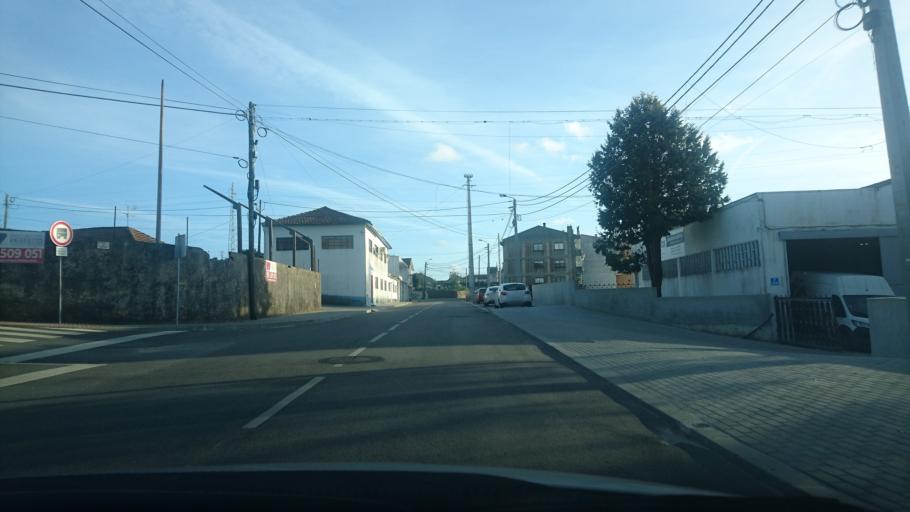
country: PT
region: Aveiro
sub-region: Santa Maria da Feira
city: Nogueira da Regedoura
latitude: 40.9930
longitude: -8.5954
